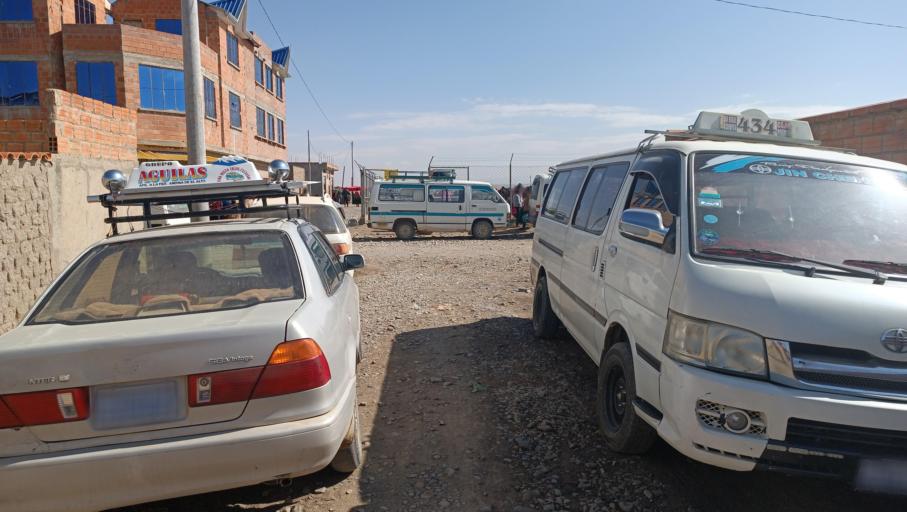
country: BO
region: La Paz
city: Batallas
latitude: -16.4378
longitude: -68.3721
